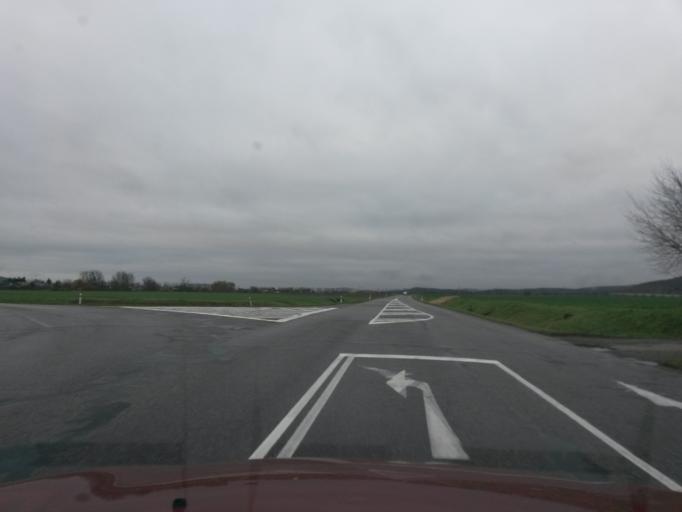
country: SK
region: Kosicky
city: Trebisov
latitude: 48.5295
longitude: 21.7318
